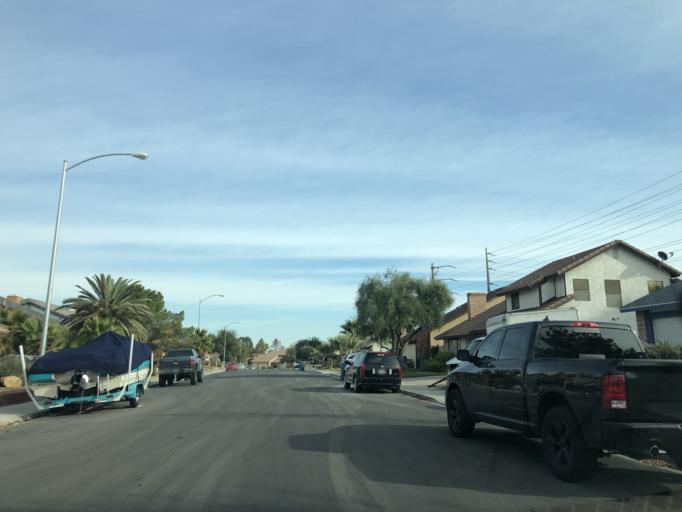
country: US
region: Nevada
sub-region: Clark County
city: Winchester
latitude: 36.1169
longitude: -115.1265
